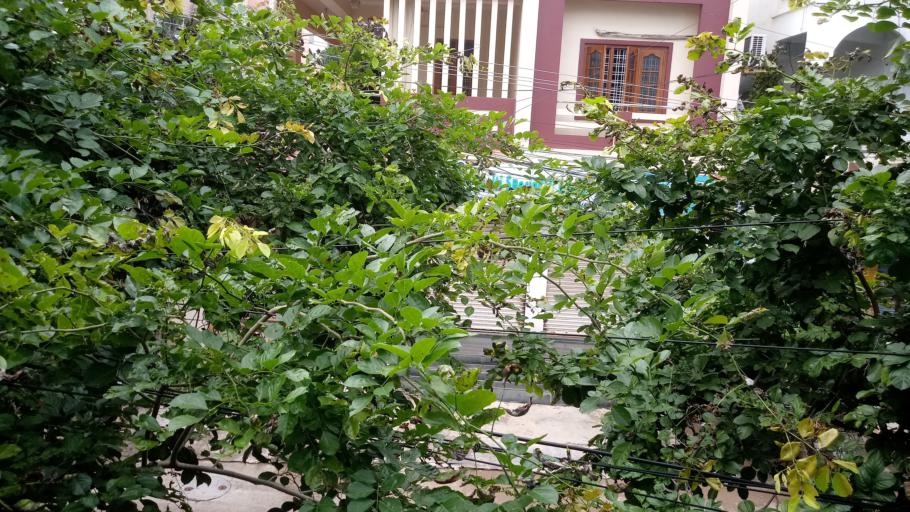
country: IN
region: Telangana
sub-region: Rangareddi
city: Lal Bahadur Nagar
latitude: 17.3695
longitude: 78.5559
